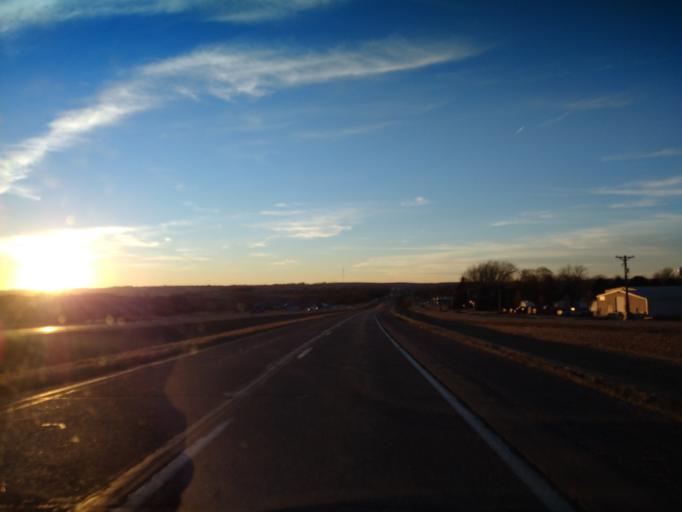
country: US
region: Iowa
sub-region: Woodbury County
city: Moville
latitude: 42.4819
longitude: -96.0565
